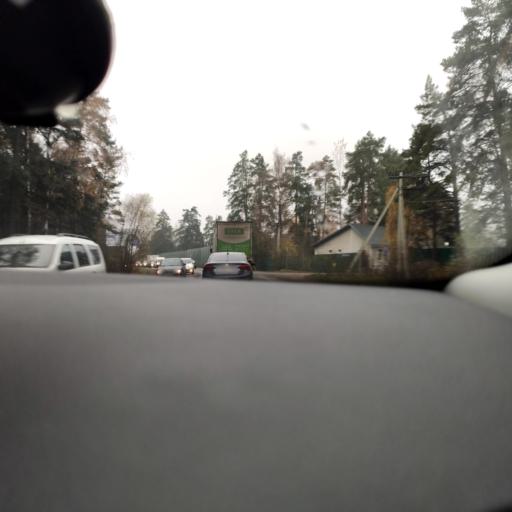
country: RU
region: Moskovskaya
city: Pavlovskaya Sloboda
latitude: 55.8055
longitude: 37.1272
